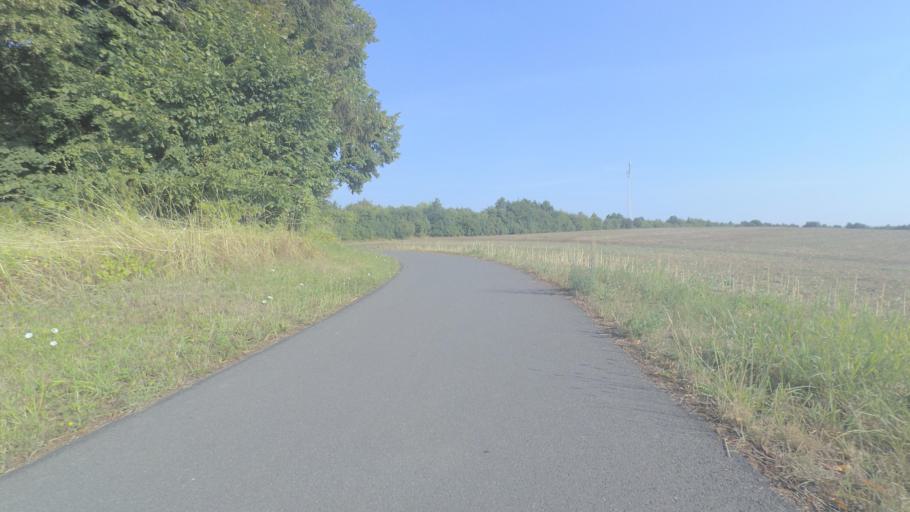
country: DE
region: Mecklenburg-Vorpommern
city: Grimmen
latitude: 54.1006
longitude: 13.0712
